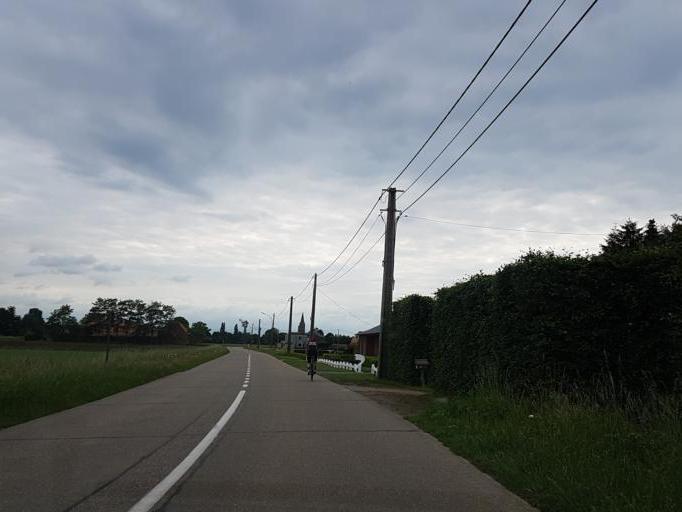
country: BE
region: Flanders
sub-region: Provincie Antwerpen
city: Rijkevorsel
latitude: 51.3555
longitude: 4.7776
